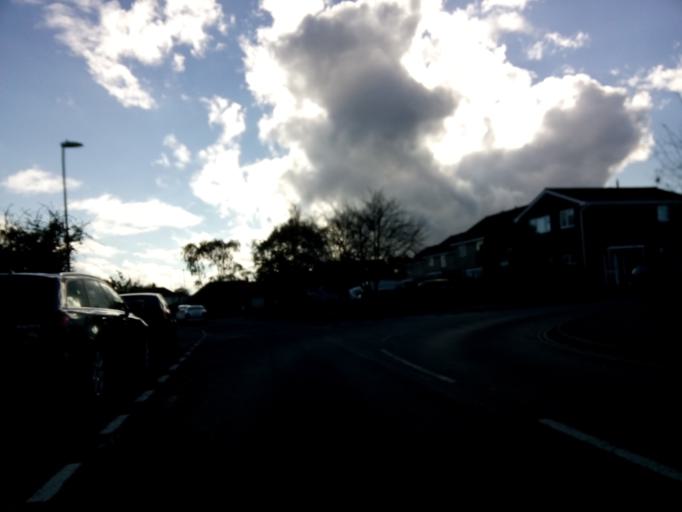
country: GB
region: England
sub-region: Suffolk
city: Kesgrave
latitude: 52.0506
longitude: 1.2091
